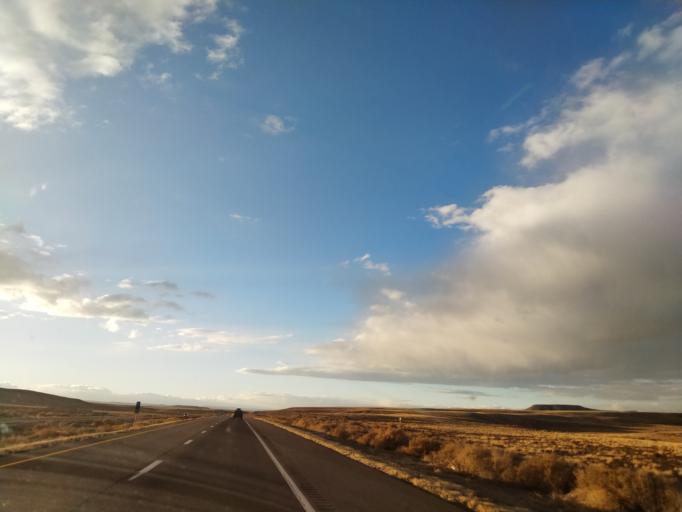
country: US
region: Colorado
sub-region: Delta County
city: Delta
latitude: 38.7657
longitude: -108.2128
